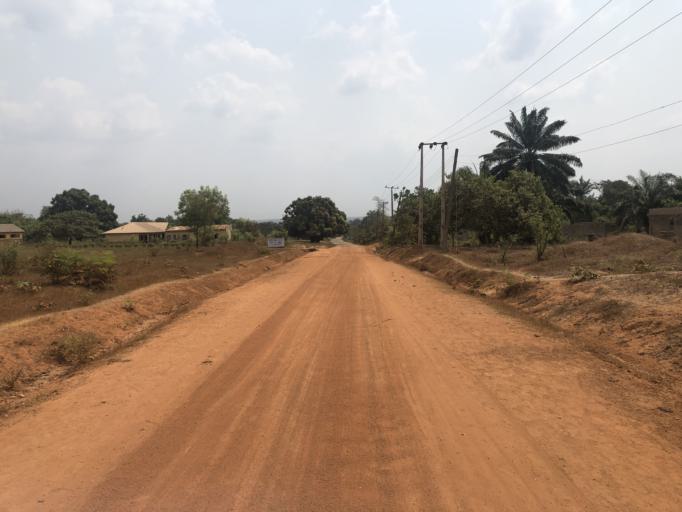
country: NG
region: Osun
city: Bode Osi
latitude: 7.7810
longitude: 4.1978
